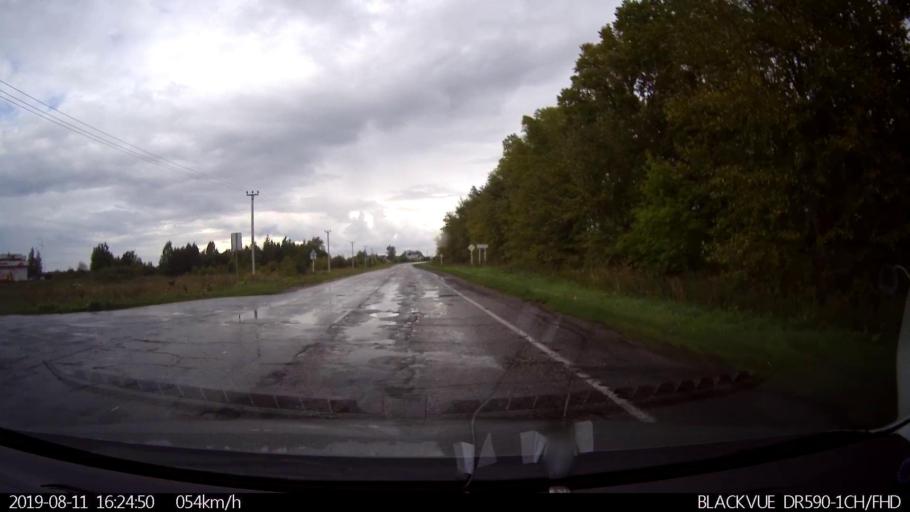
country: RU
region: Ulyanovsk
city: Mayna
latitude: 54.1029
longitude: 47.5986
